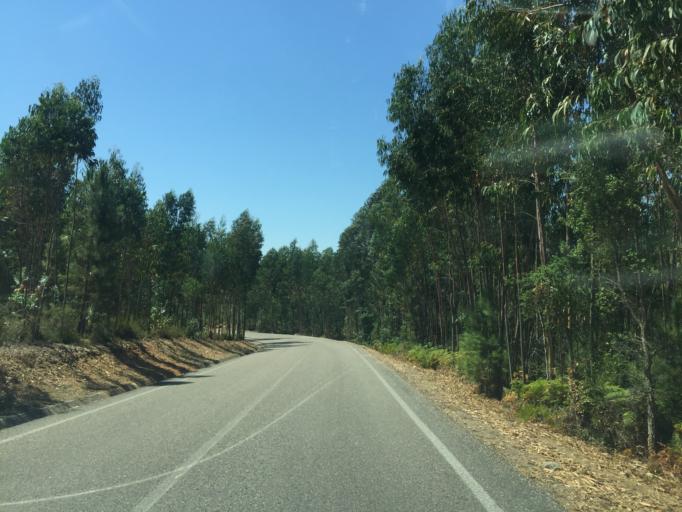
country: PT
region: Santarem
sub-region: Ferreira do Zezere
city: Ferreira do Zezere
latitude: 39.5903
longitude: -8.2992
